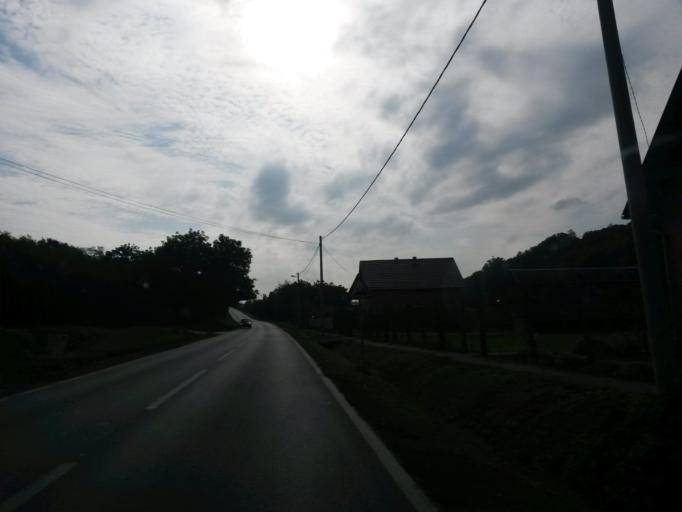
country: HR
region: Vukovarsko-Srijemska
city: Bapska
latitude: 45.2318
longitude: 19.2984
